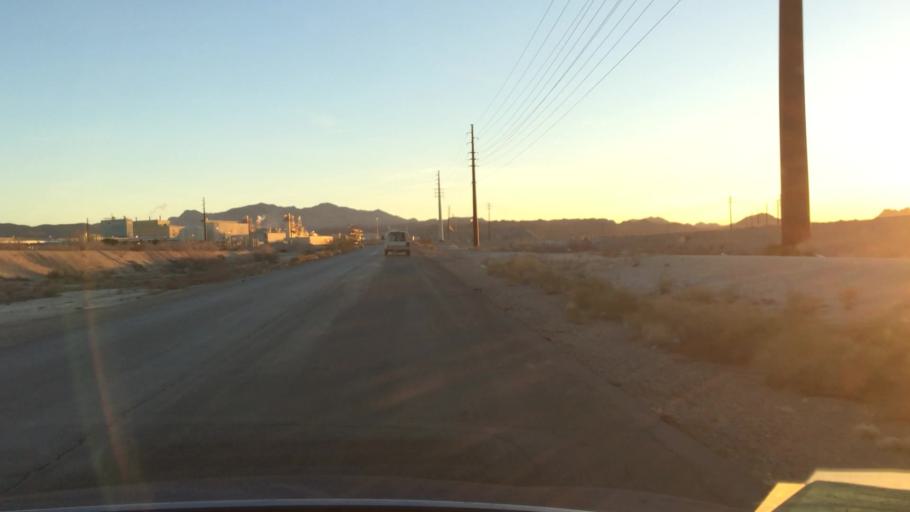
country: US
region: Nevada
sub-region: Clark County
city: Nellis Air Force Base
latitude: 36.2222
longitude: -114.8844
